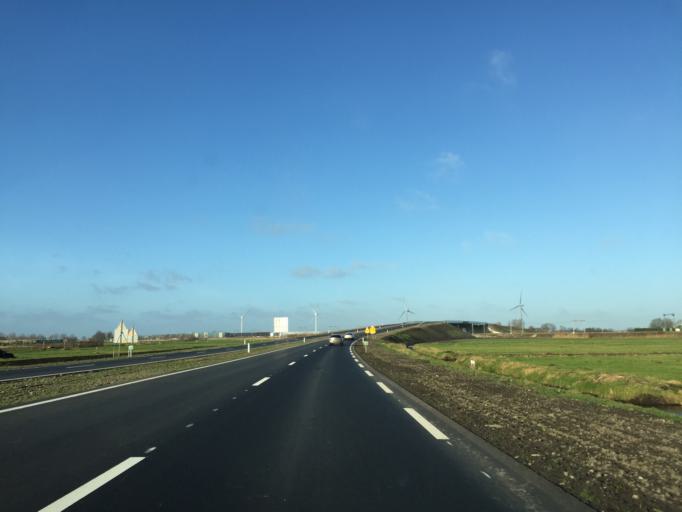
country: NL
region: South Holland
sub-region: Gemeente Waddinxveen
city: Waddinxveen
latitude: 52.0059
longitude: 4.6486
